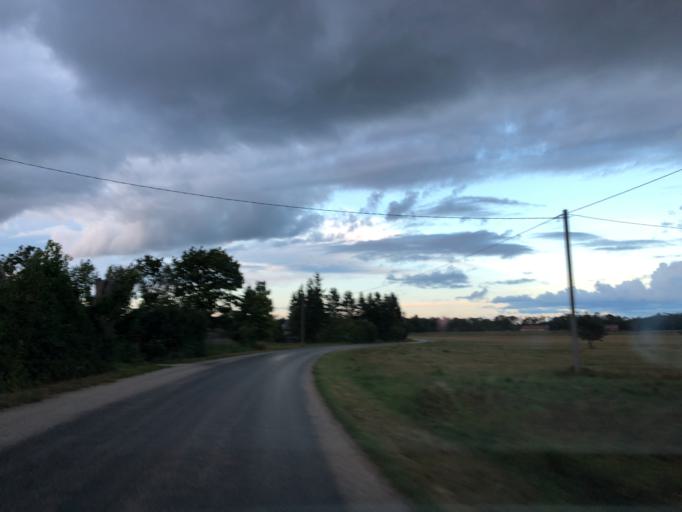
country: EE
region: Laeaene
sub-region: Ridala Parish
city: Uuemoisa
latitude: 58.8767
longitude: 23.6203
